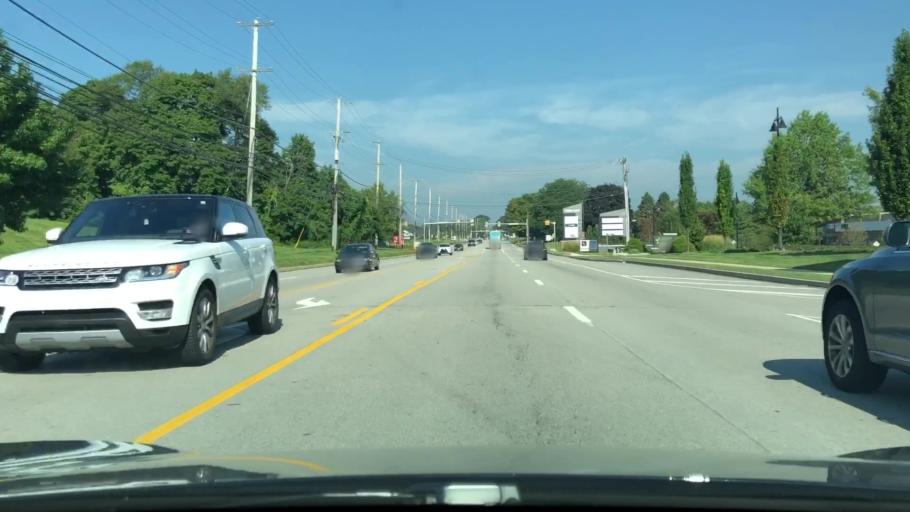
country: US
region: Pennsylvania
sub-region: Montgomery County
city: Horsham
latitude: 40.1579
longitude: -75.1448
